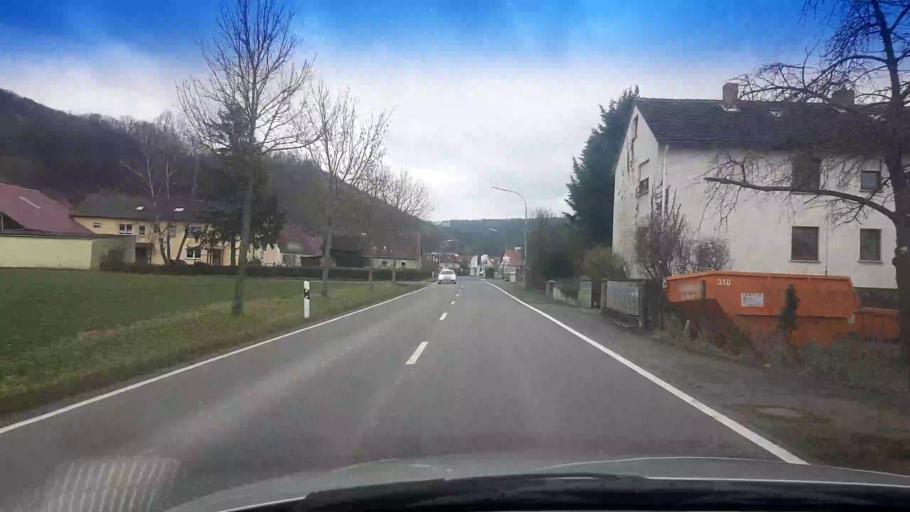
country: DE
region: Bavaria
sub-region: Regierungsbezirk Unterfranken
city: Knetzgau
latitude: 49.9700
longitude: 10.5628
